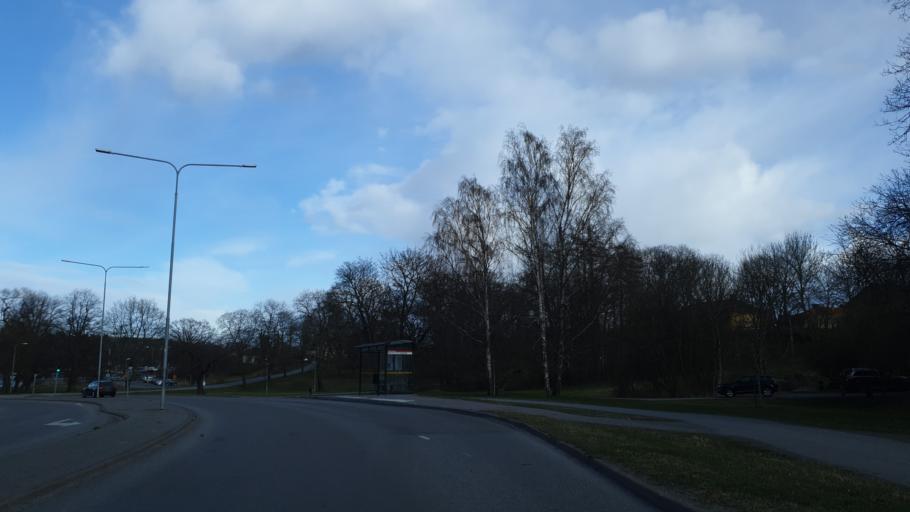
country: SE
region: Stockholm
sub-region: Lidingo
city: Lidingoe
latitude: 59.3669
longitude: 18.1523
